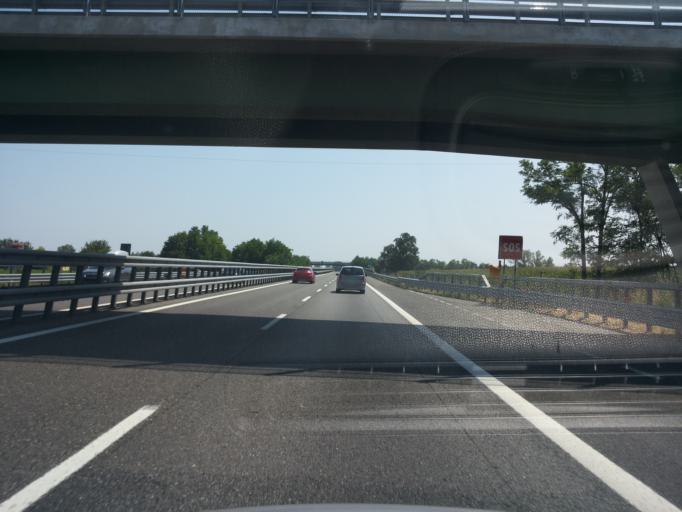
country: IT
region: Emilia-Romagna
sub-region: Provincia di Piacenza
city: Rottofreno
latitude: 45.0666
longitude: 9.5251
